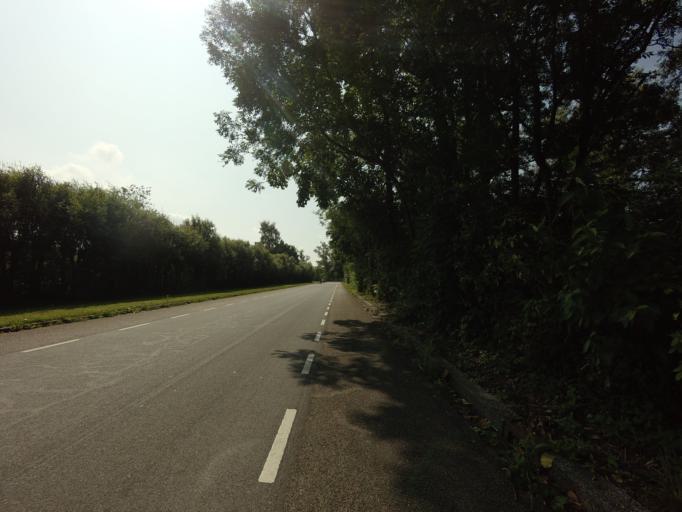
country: NL
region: South Holland
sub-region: Gemeente Sliedrecht
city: Sliedrecht
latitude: 51.8123
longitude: 4.7502
